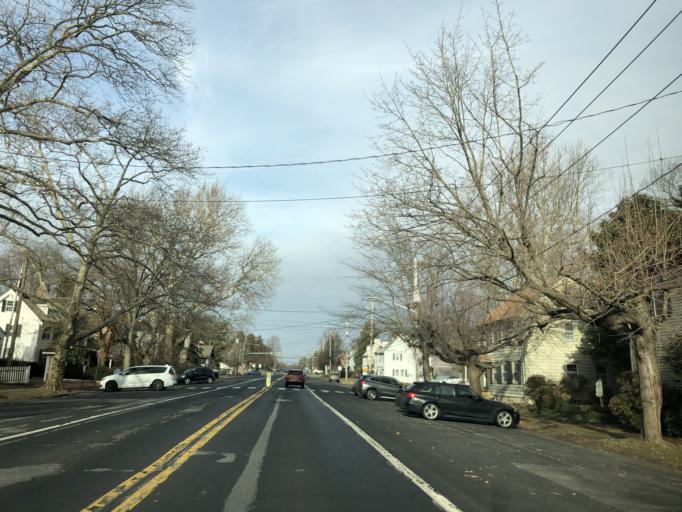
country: US
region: Delaware
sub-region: New Castle County
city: Middletown
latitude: 39.4552
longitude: -75.6585
